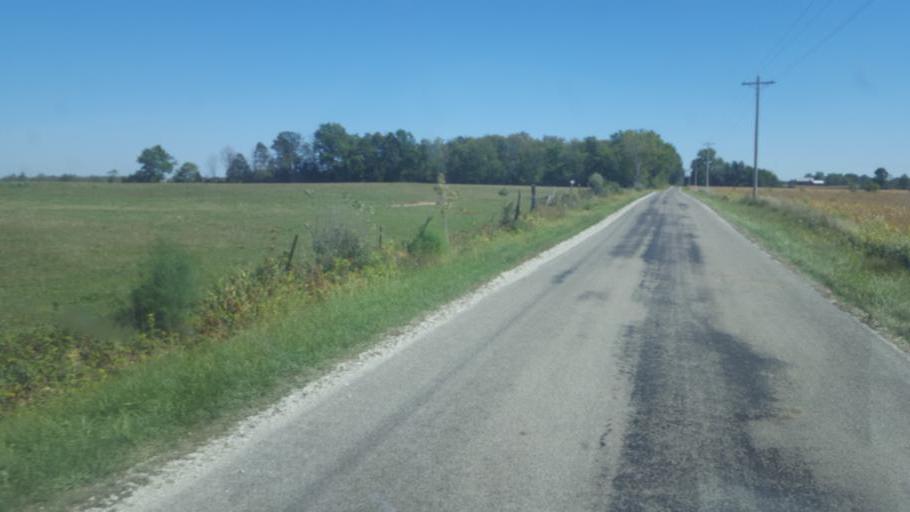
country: US
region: Ohio
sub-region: Huron County
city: Willard
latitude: 40.9457
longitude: -82.8093
